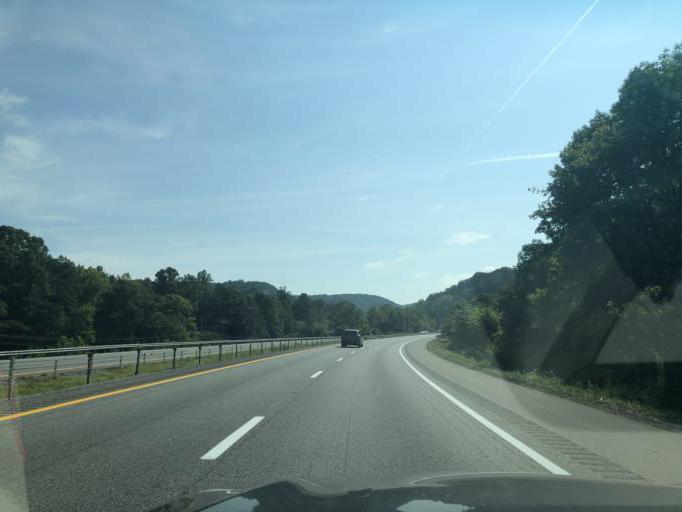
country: US
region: Georgia
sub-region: Dade County
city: Trenton
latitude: 34.9883
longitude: -85.4955
